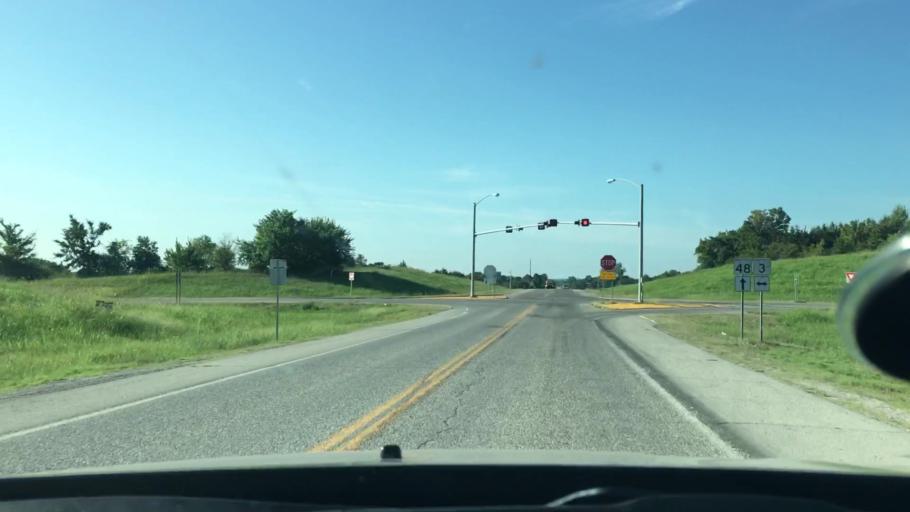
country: US
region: Oklahoma
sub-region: Coal County
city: Coalgate
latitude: 34.6118
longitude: -96.4244
